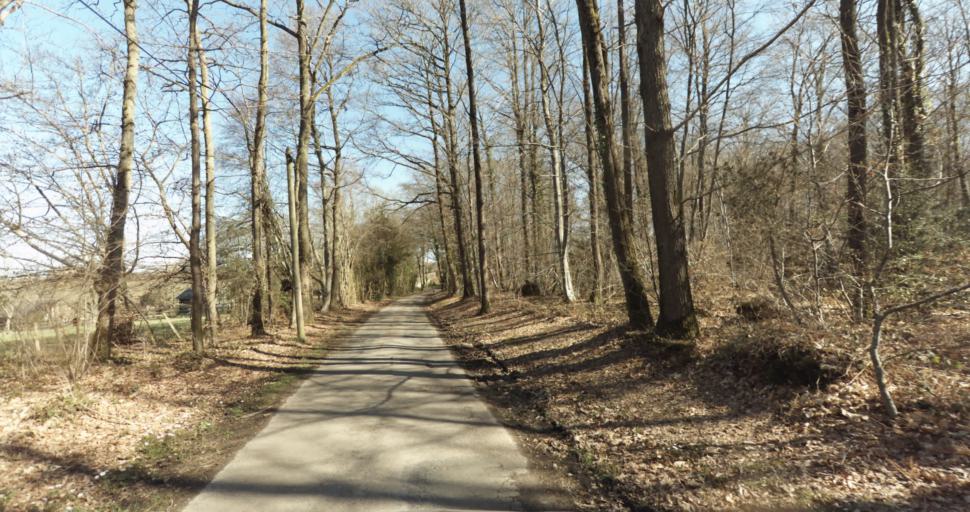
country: FR
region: Lower Normandy
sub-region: Departement du Calvados
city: Livarot
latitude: 48.9769
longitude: 0.0814
